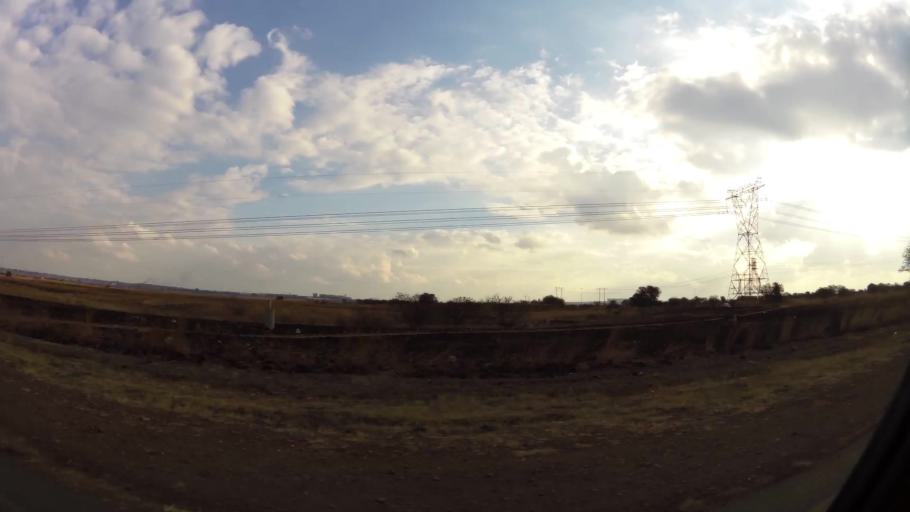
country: ZA
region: Gauteng
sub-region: Sedibeng District Municipality
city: Vereeniging
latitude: -26.6465
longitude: 27.8757
